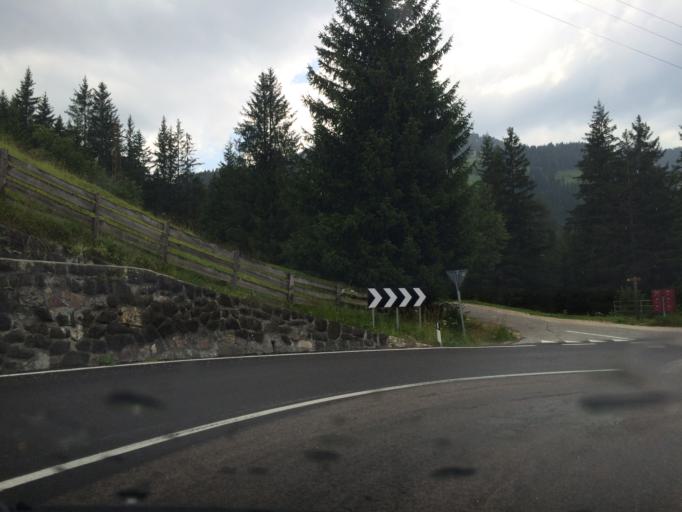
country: IT
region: Trentino-Alto Adige
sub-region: Bolzano
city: Badia
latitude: 46.6190
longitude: 11.8925
